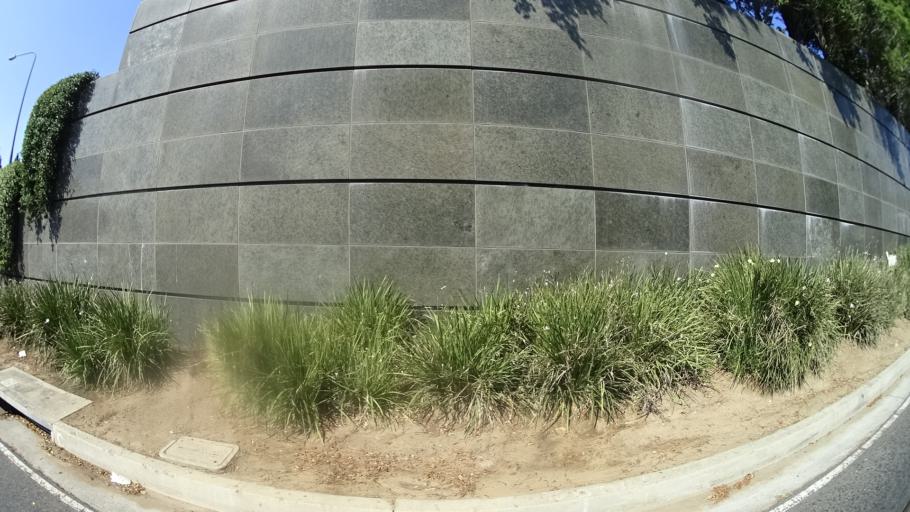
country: US
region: California
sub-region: Los Angeles County
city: Universal City
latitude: 34.1380
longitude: -118.3624
